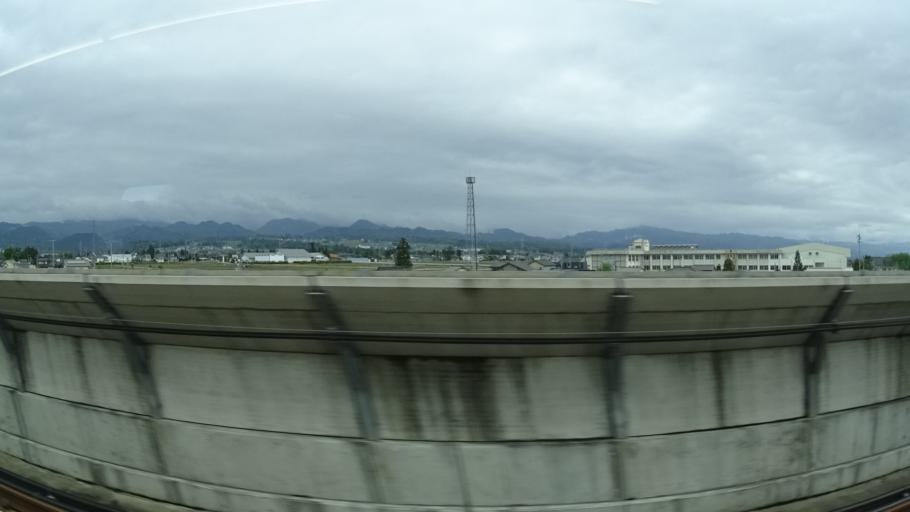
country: JP
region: Toyama
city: Namerikawa
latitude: 36.7598
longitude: 137.3739
